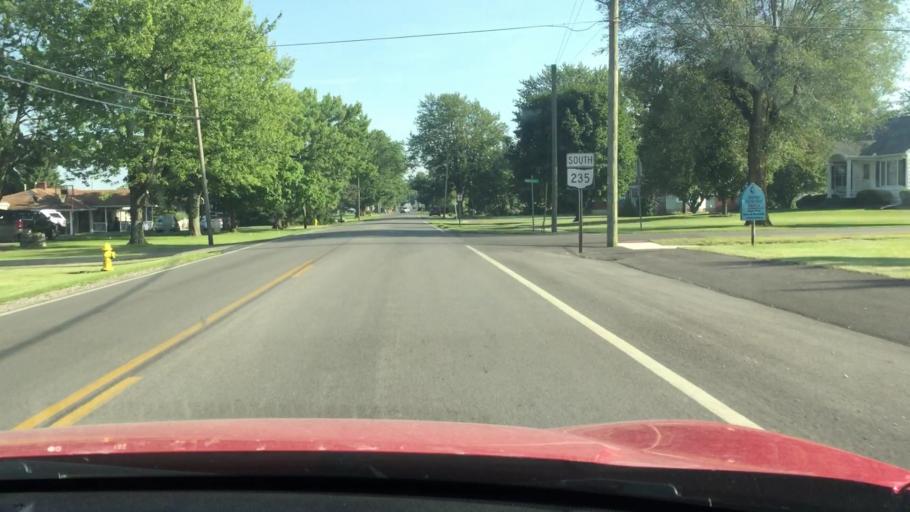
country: US
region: Ohio
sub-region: Hardin County
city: Ada
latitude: 40.7109
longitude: -83.8422
